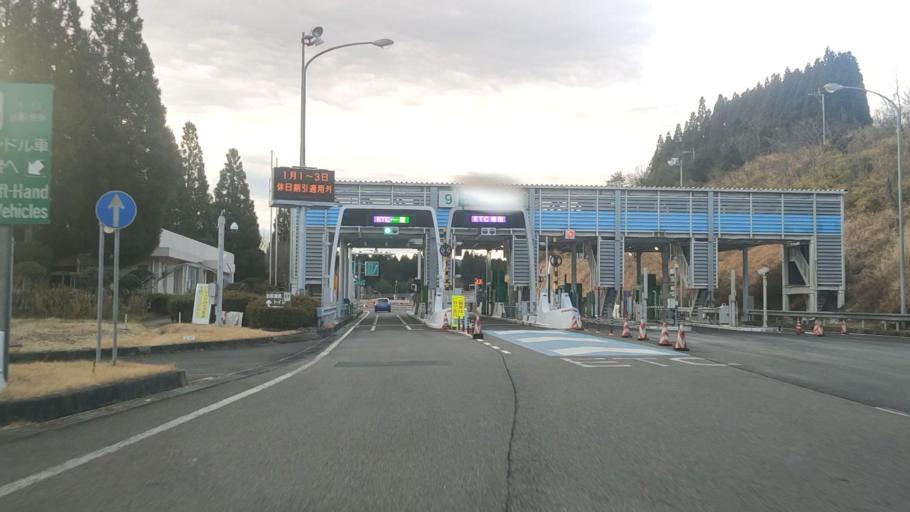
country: JP
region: Oita
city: Beppu
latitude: 33.2597
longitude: 131.3282
